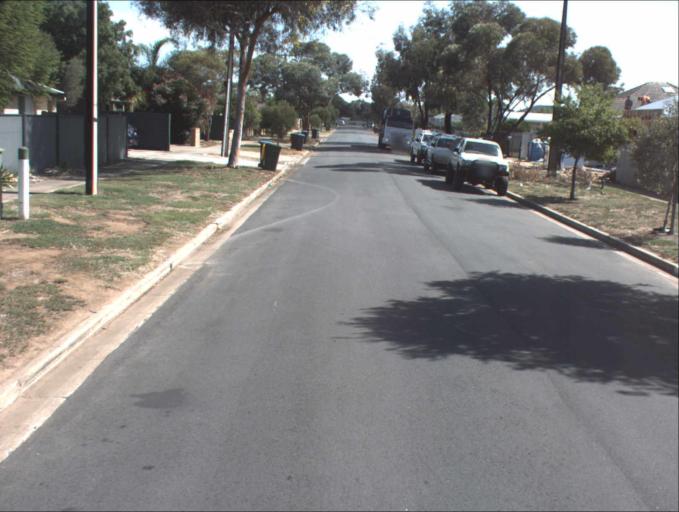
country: AU
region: South Australia
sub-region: Prospect
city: Prospect
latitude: -34.8810
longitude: 138.5771
